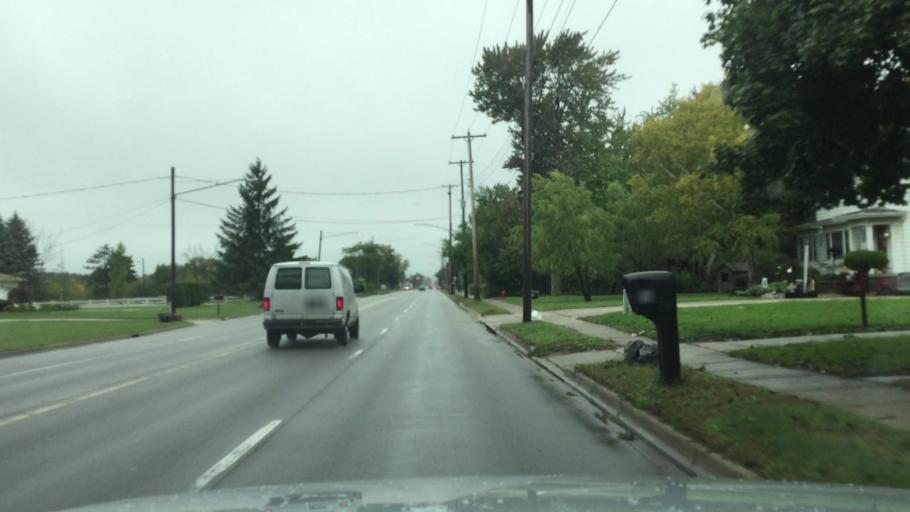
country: US
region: Michigan
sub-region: Saginaw County
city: Buena Vista
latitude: 43.4037
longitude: -83.9142
